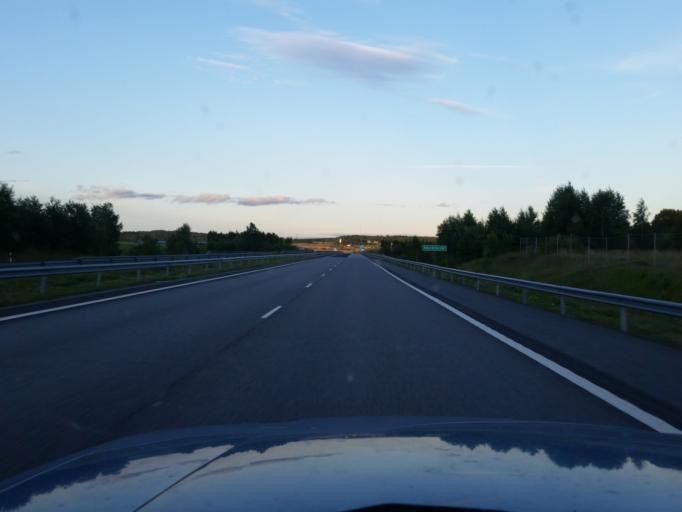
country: FI
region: Varsinais-Suomi
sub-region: Salo
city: Halikko
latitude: 60.4301
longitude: 23.0047
